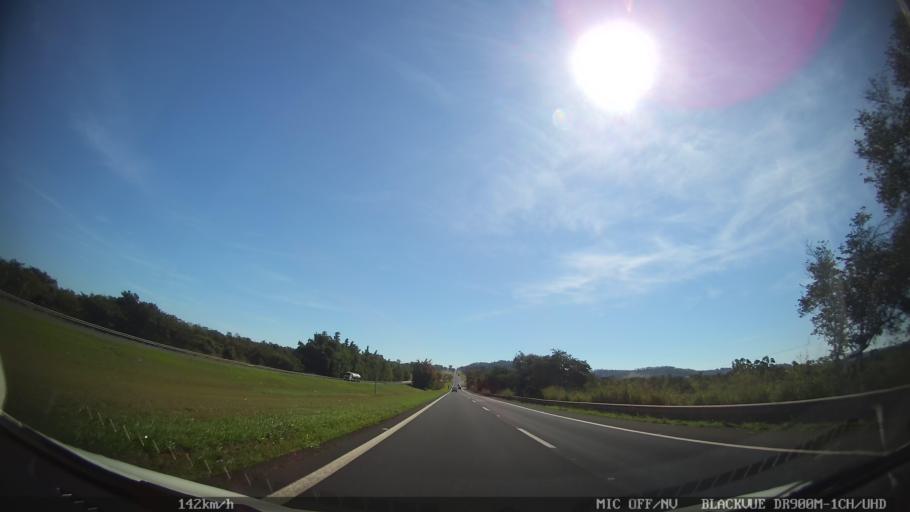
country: BR
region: Sao Paulo
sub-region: Santa Rita Do Passa Quatro
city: Santa Rita do Passa Quatro
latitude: -21.7348
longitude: -47.5833
